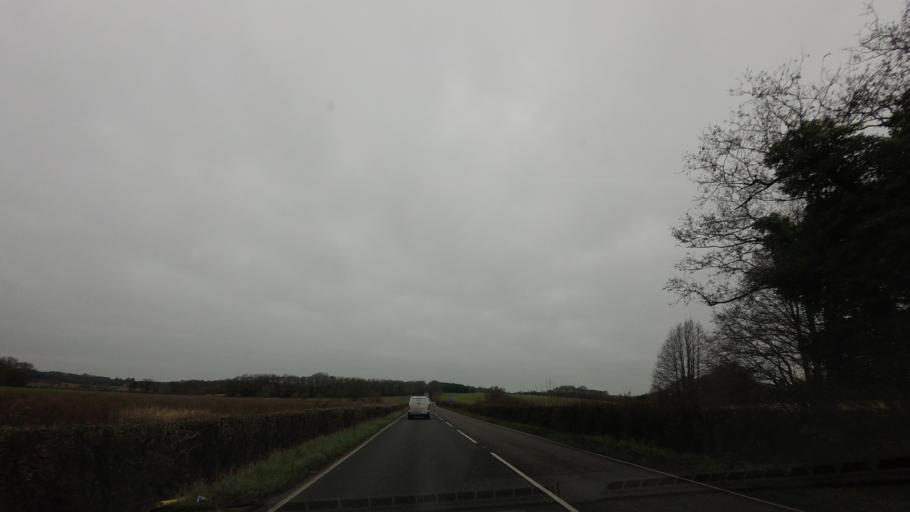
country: GB
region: England
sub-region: East Sussex
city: Battle
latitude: 50.9313
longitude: 0.5241
